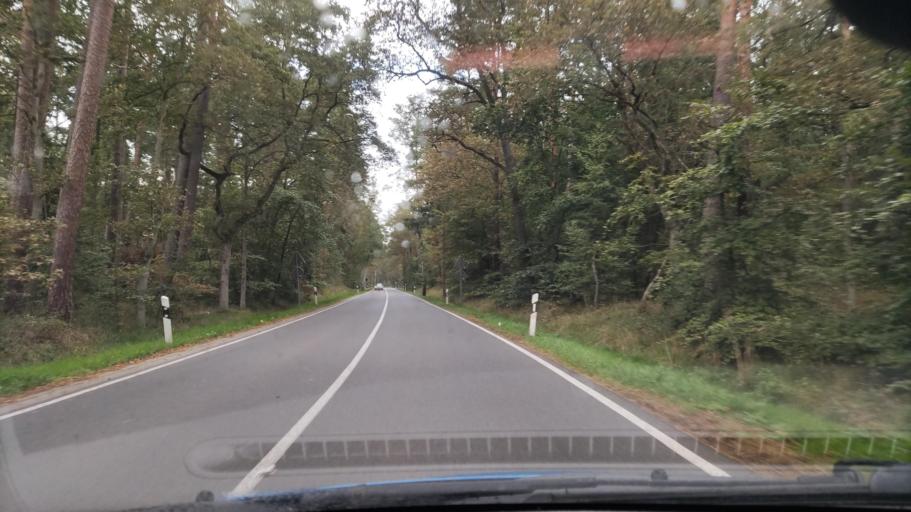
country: DE
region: Brandenburg
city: Lanz
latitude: 53.0007
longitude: 11.5531
